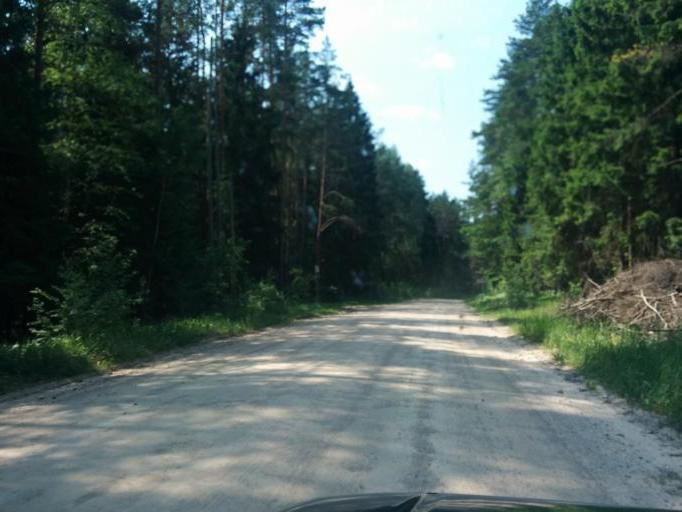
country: LV
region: Baldone
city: Baldone
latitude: 56.7460
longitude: 24.4444
